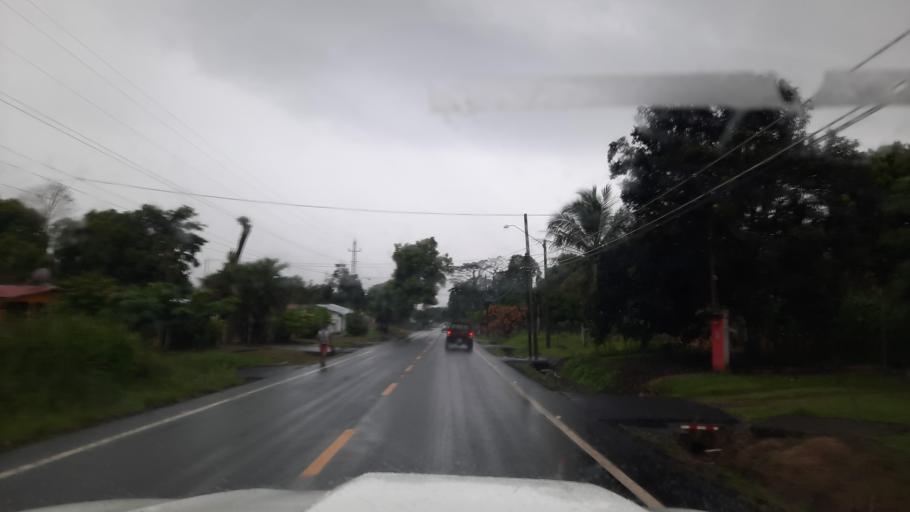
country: PA
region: Chiriqui
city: Sortova
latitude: 8.5463
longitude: -82.6250
